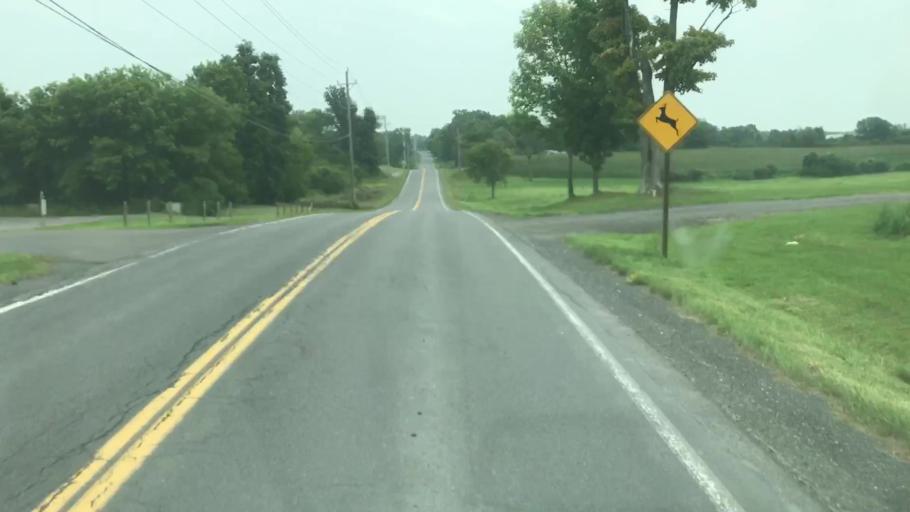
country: US
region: New York
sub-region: Cayuga County
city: Melrose Park
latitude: 42.9535
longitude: -76.5043
